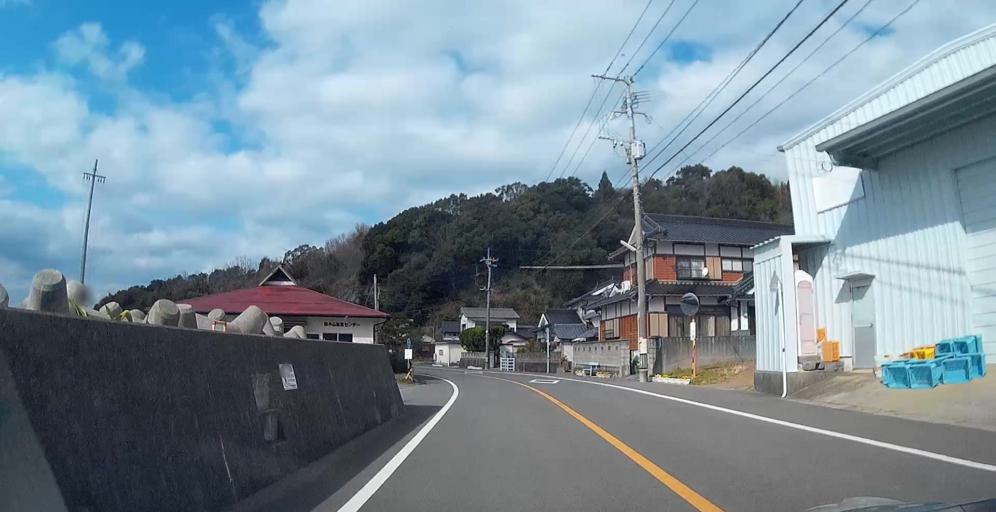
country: JP
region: Kumamoto
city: Minamata
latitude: 32.3110
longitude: 130.4724
